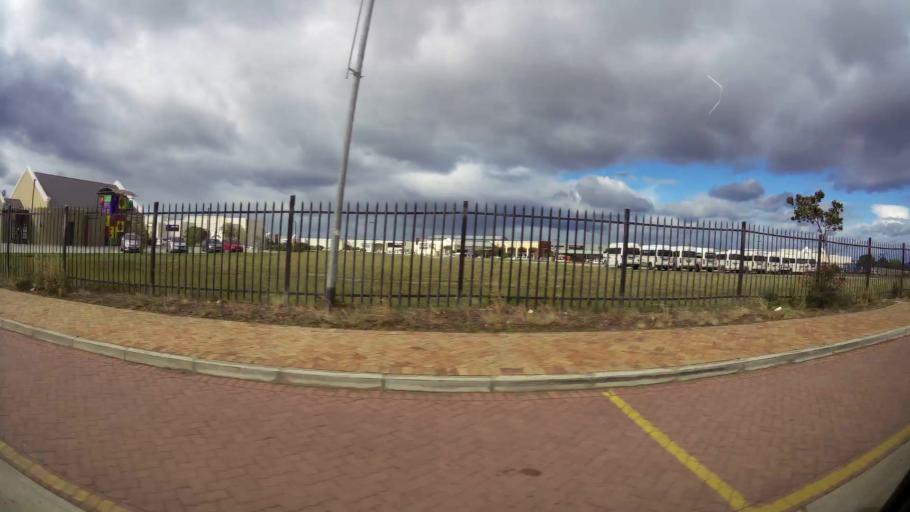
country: ZA
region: Western Cape
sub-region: Eden District Municipality
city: George
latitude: -33.9859
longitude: 22.5010
